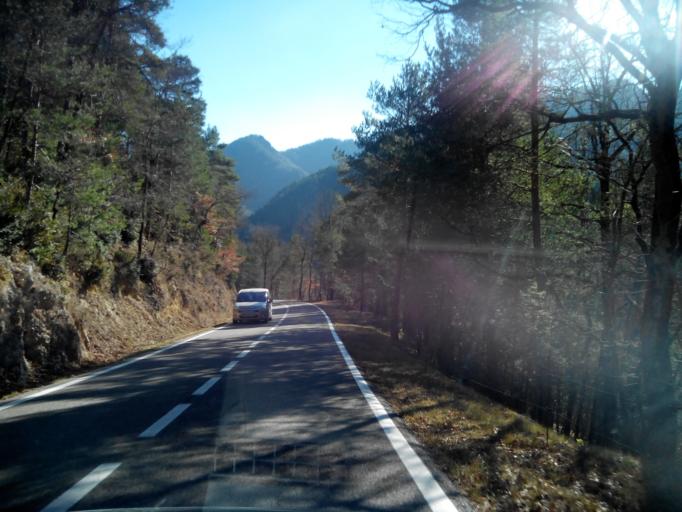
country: ES
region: Catalonia
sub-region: Provincia de Barcelona
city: Capolat
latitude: 42.1034
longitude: 1.7384
